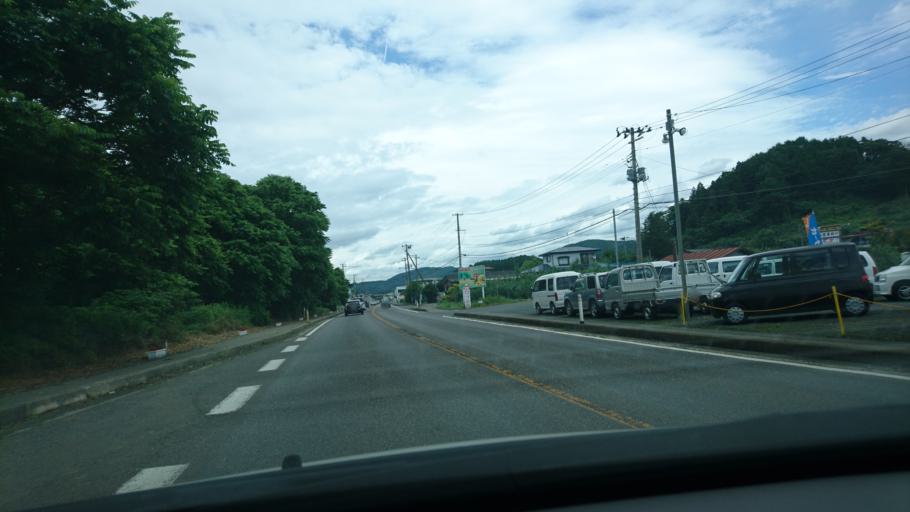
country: JP
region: Iwate
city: Morioka-shi
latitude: 39.6253
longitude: 141.1833
